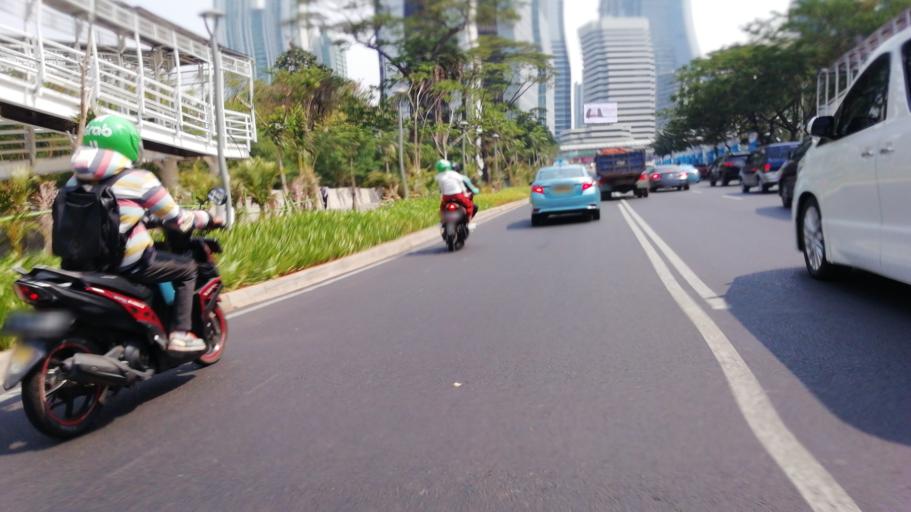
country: ID
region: Jakarta Raya
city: Jakarta
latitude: -6.2057
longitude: 106.8224
